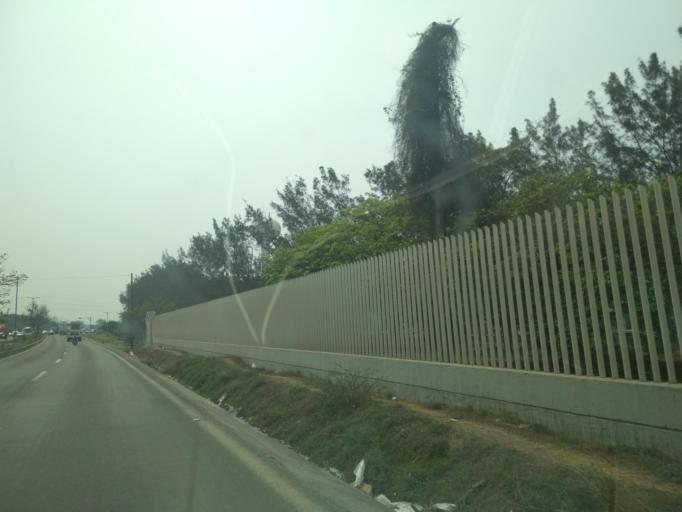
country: MX
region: Veracruz
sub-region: Veracruz
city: Oasis
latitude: 19.1755
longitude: -96.2391
